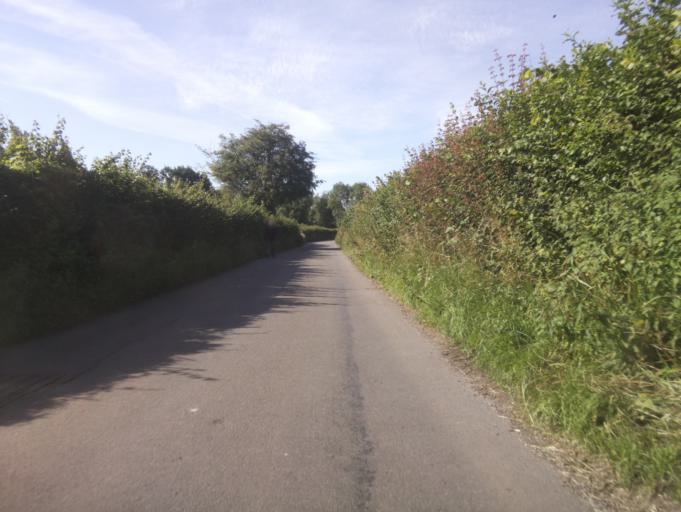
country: GB
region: England
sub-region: South Gloucestershire
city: Bitton
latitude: 51.4302
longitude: -2.4539
